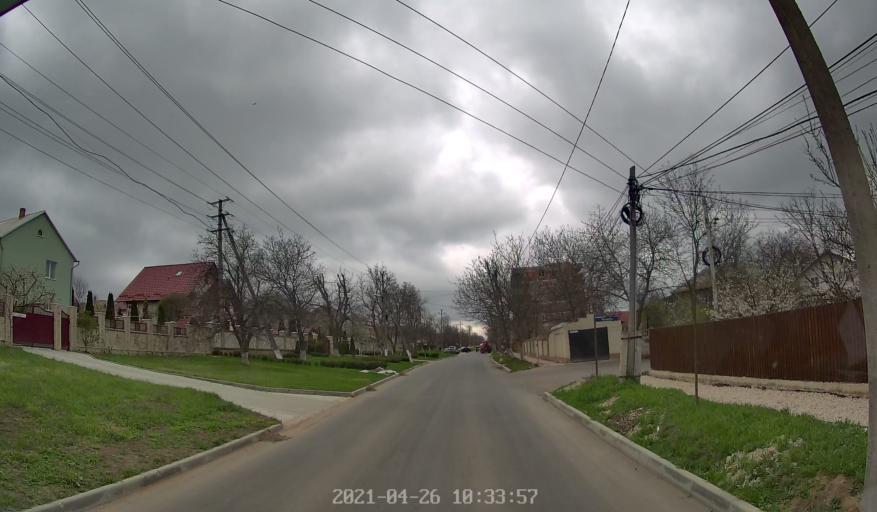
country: MD
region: Chisinau
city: Cricova
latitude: 47.1302
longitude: 28.8623
